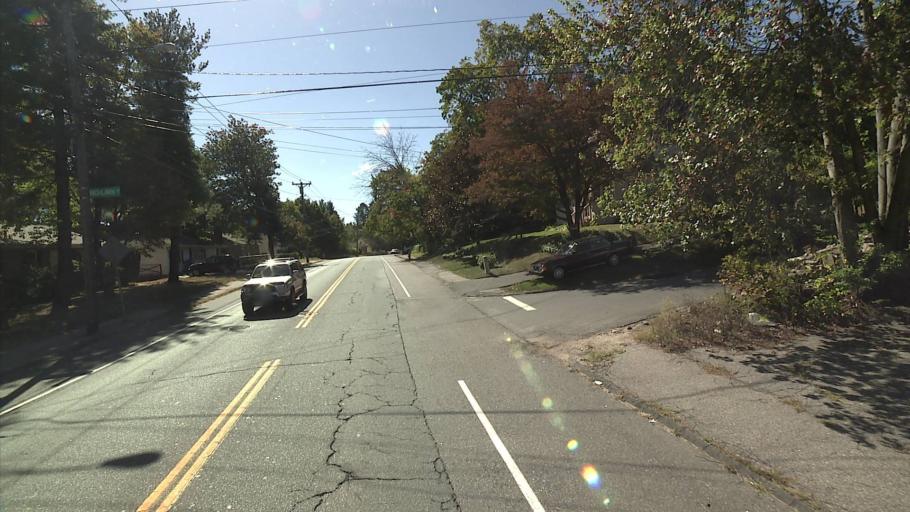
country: US
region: Connecticut
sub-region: New Haven County
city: Wolcott
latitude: 41.5599
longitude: -73.0051
